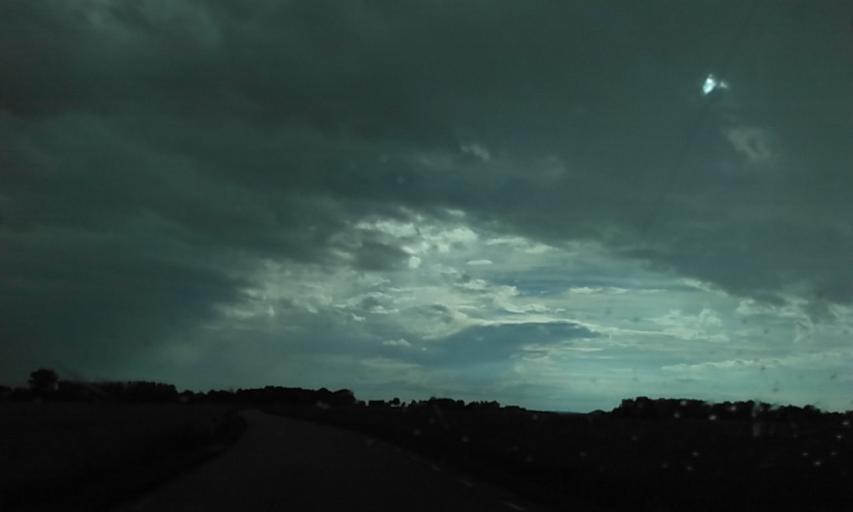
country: SE
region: Vaestra Goetaland
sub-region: Grastorps Kommun
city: Graestorp
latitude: 58.4380
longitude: 12.7531
